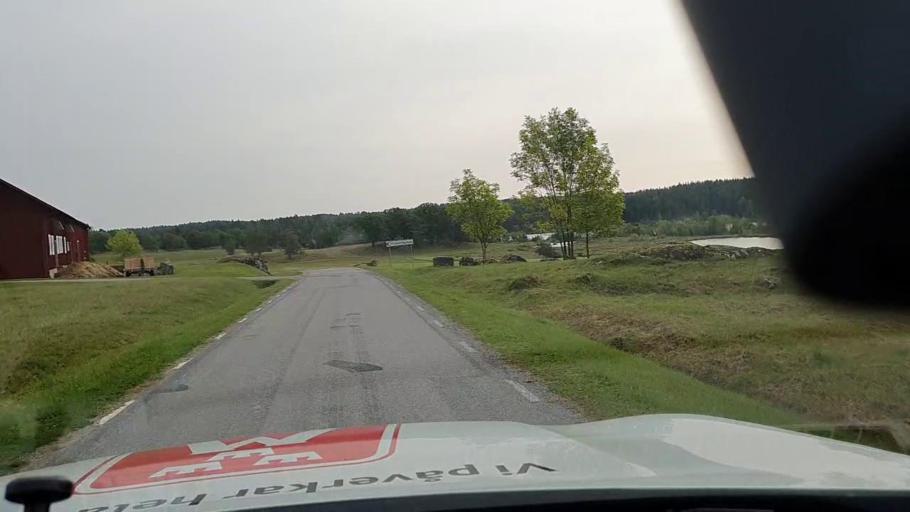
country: SE
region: Soedermanland
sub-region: Nykopings Kommun
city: Stigtomta
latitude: 58.9823
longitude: 16.9346
